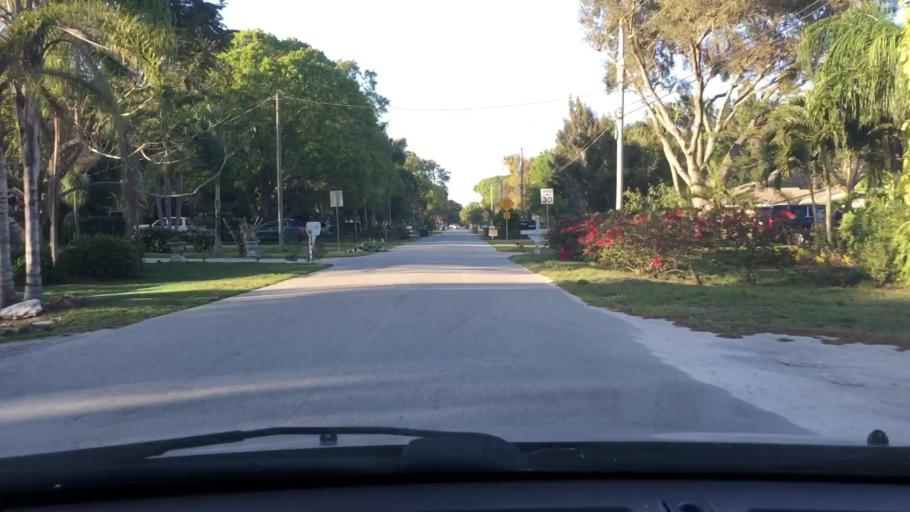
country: US
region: Florida
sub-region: Indian River County
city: Vero Beach South
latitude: 27.6424
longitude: -80.4409
